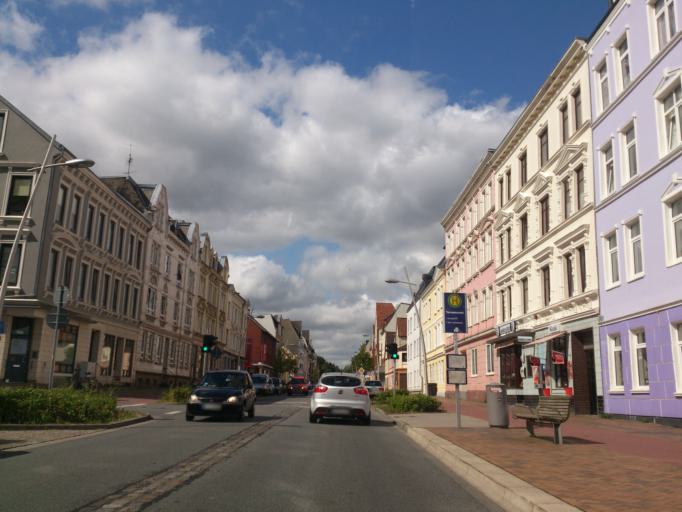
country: DE
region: Schleswig-Holstein
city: Flensburg
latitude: 54.8031
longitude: 9.4243
